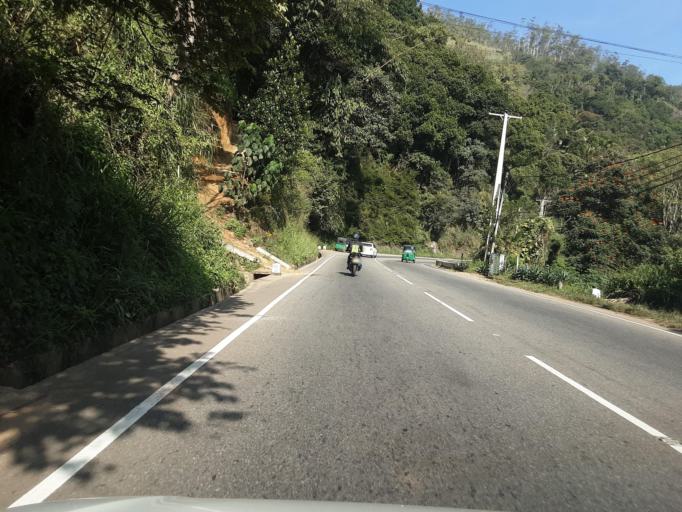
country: LK
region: Uva
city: Badulla
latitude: 6.9784
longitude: 81.0442
